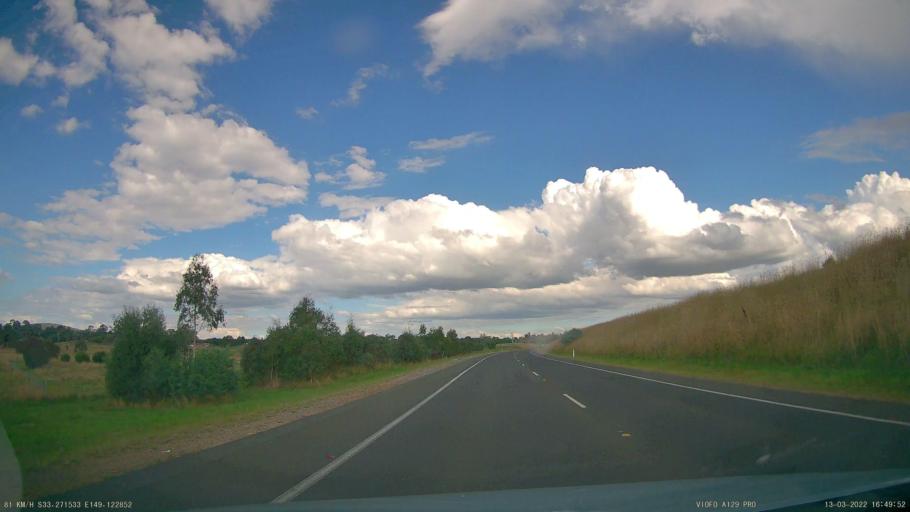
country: AU
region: New South Wales
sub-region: Orange Municipality
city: Orange
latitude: -33.2717
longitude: 149.1230
